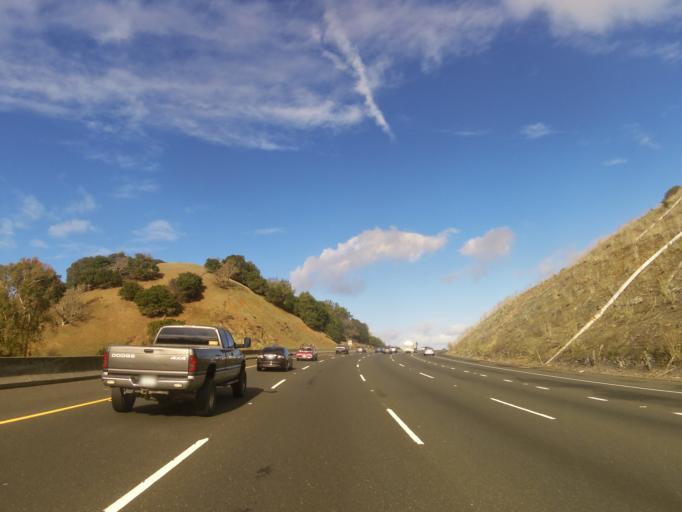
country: US
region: California
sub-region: Marin County
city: Lucas Valley-Marinwood
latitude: 38.0404
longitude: -122.5368
